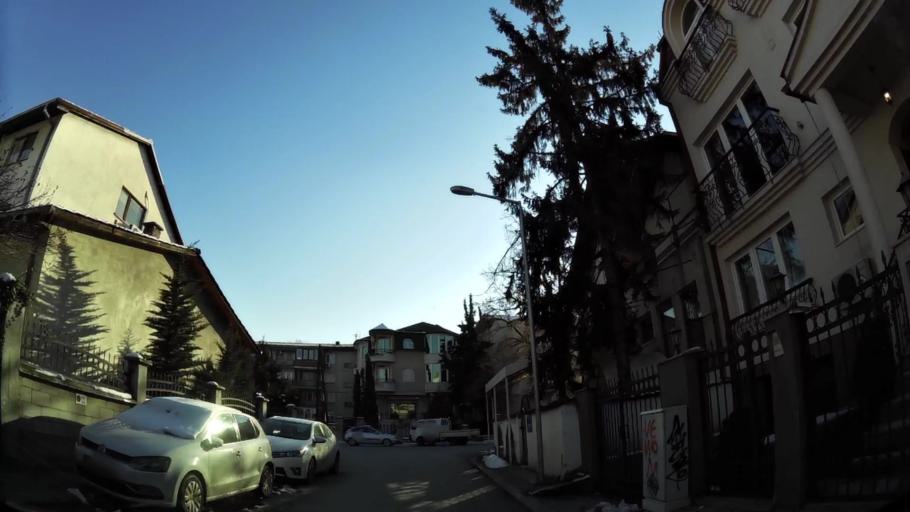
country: MK
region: Karpos
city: Skopje
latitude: 42.0011
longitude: 21.3986
